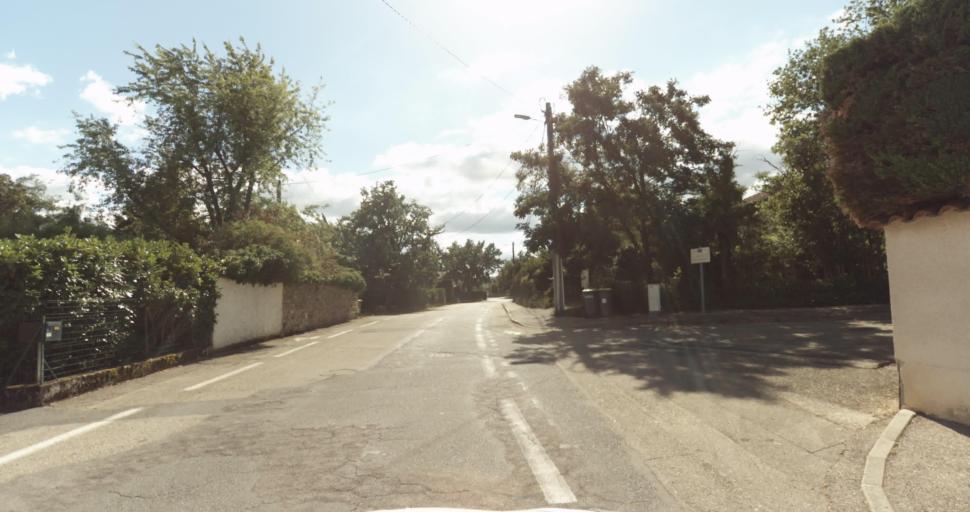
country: FR
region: Rhone-Alpes
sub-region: Departement du Rhone
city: Chaponost
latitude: 45.7091
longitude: 4.7388
